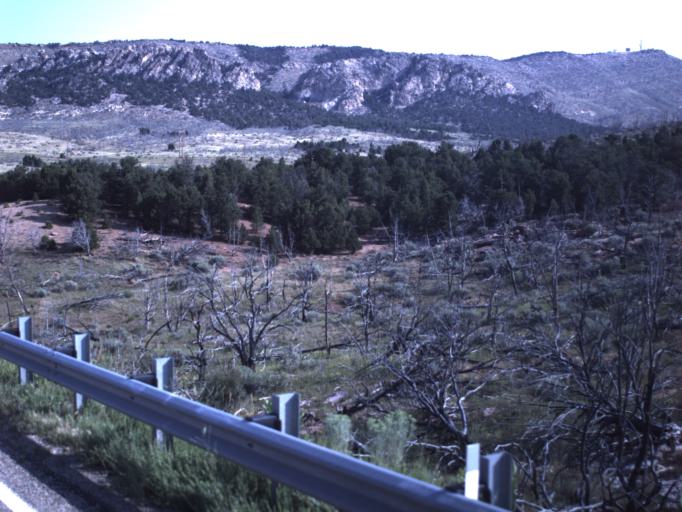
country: US
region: Utah
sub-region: Daggett County
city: Manila
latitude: 40.9424
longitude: -109.4270
